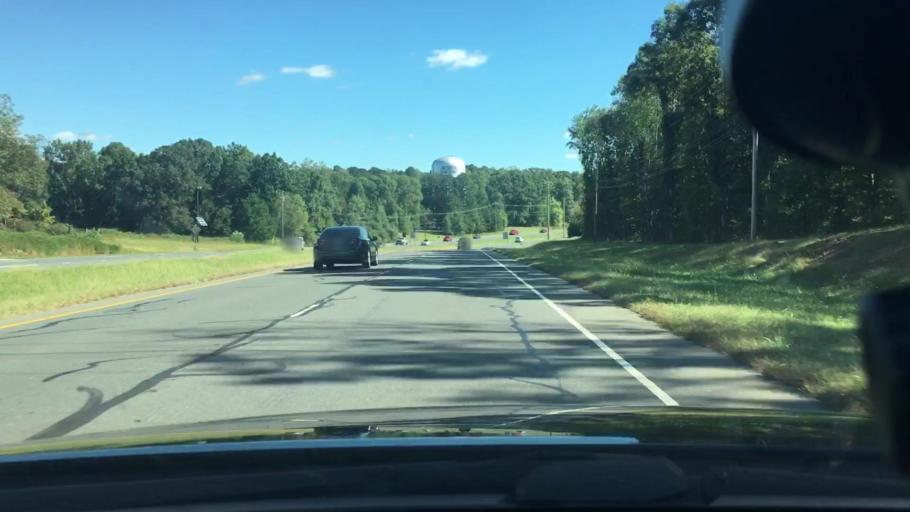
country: US
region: North Carolina
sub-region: Stanly County
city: Locust
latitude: 35.2681
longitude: -80.3787
